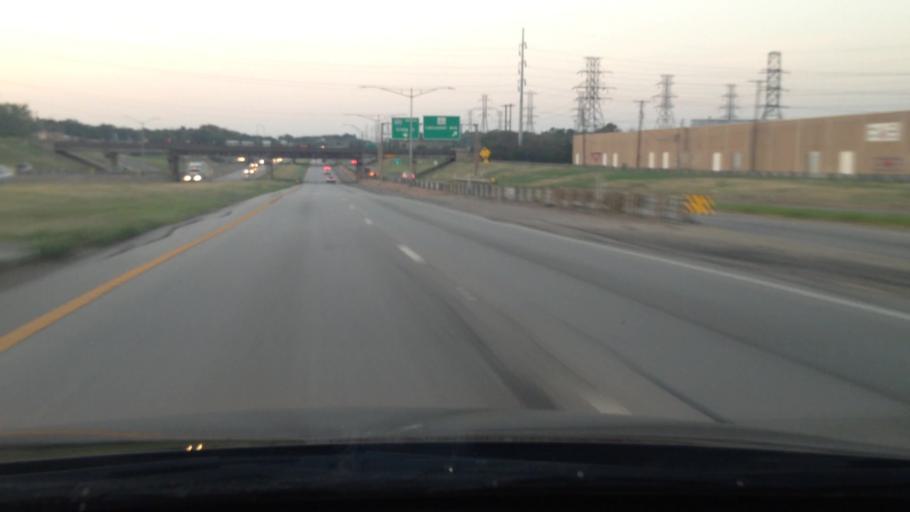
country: US
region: Texas
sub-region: Tarrant County
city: Pantego
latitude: 32.7310
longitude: -97.2251
